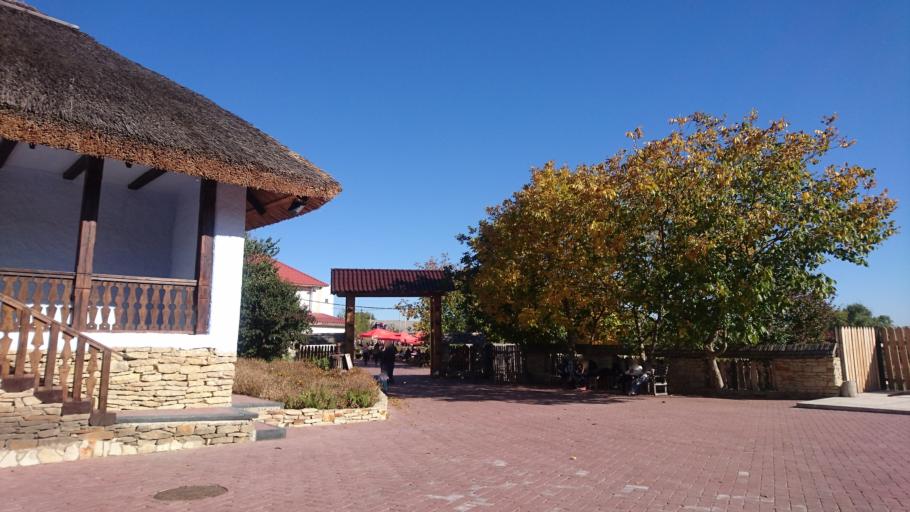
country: MD
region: Chisinau
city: Singera
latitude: 46.8393
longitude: 29.0249
